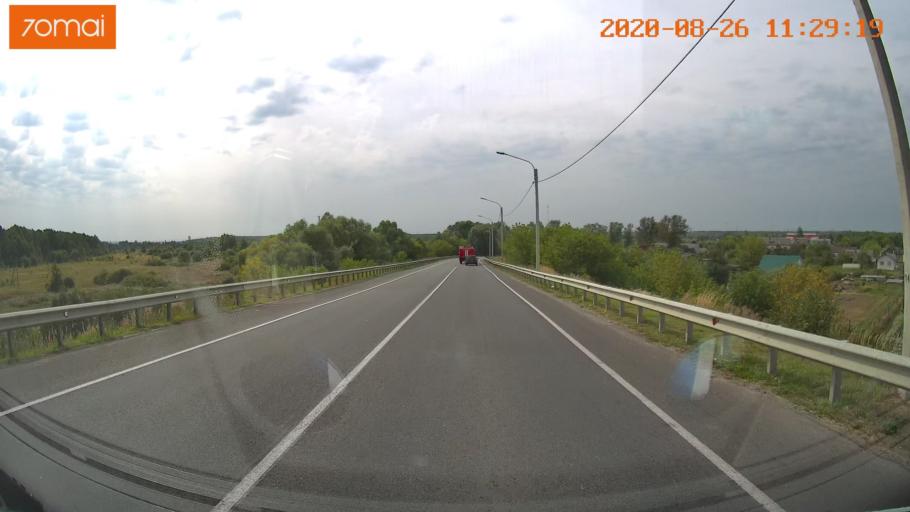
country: RU
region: Rjazan
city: Shilovo
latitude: 54.3209
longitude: 40.9000
